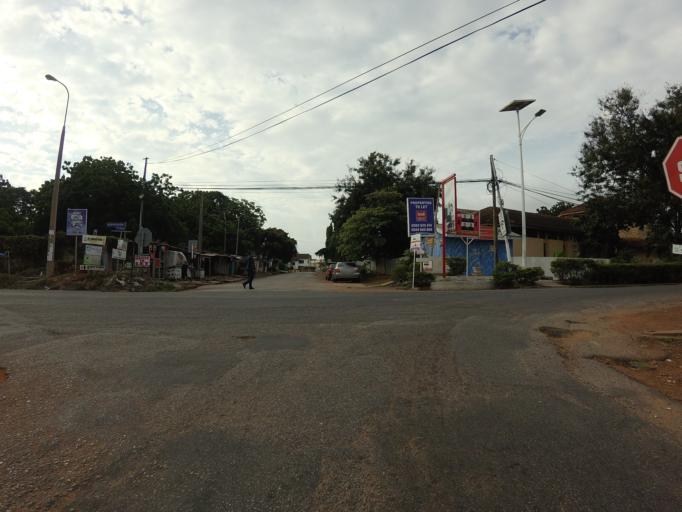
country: GH
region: Greater Accra
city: Accra
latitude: 5.5811
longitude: -0.1707
